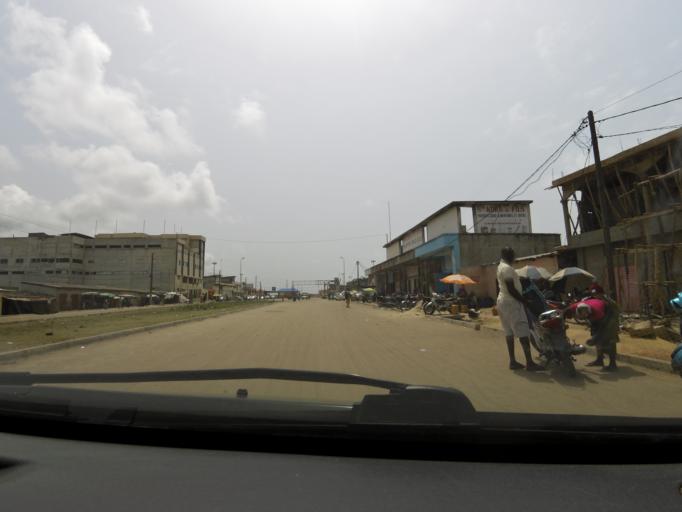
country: BJ
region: Queme
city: Porto-Novo
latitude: 6.3787
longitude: 2.7003
